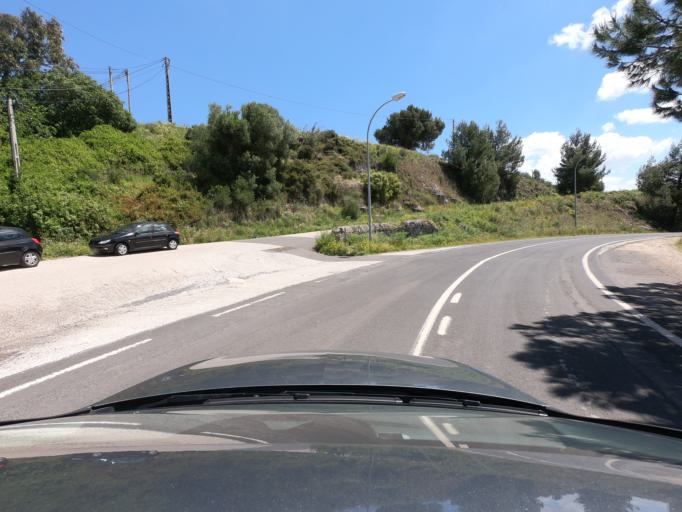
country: PT
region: Lisbon
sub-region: Oeiras
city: Quejas
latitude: 38.7174
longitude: -9.2746
